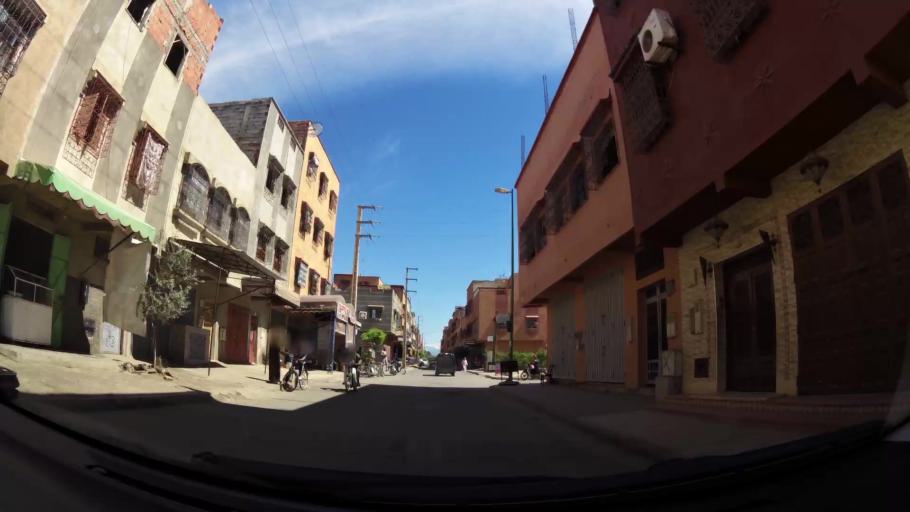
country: MA
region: Marrakech-Tensift-Al Haouz
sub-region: Marrakech
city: Marrakesh
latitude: 31.5973
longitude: -7.9590
